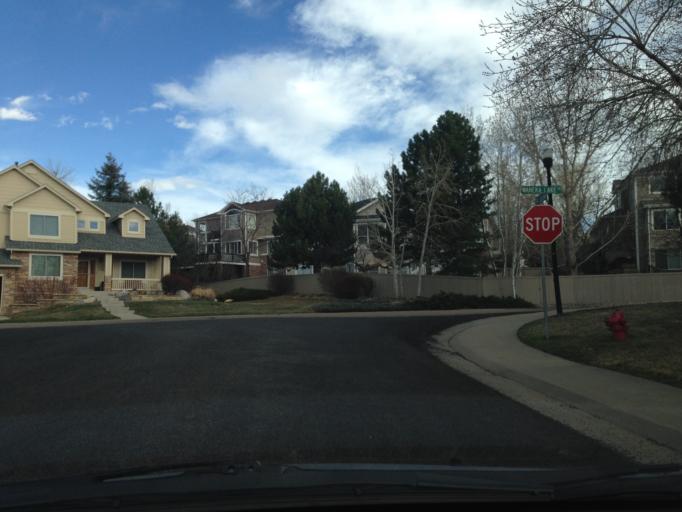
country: US
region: Colorado
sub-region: Boulder County
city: Louisville
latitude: 39.9992
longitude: -105.1258
